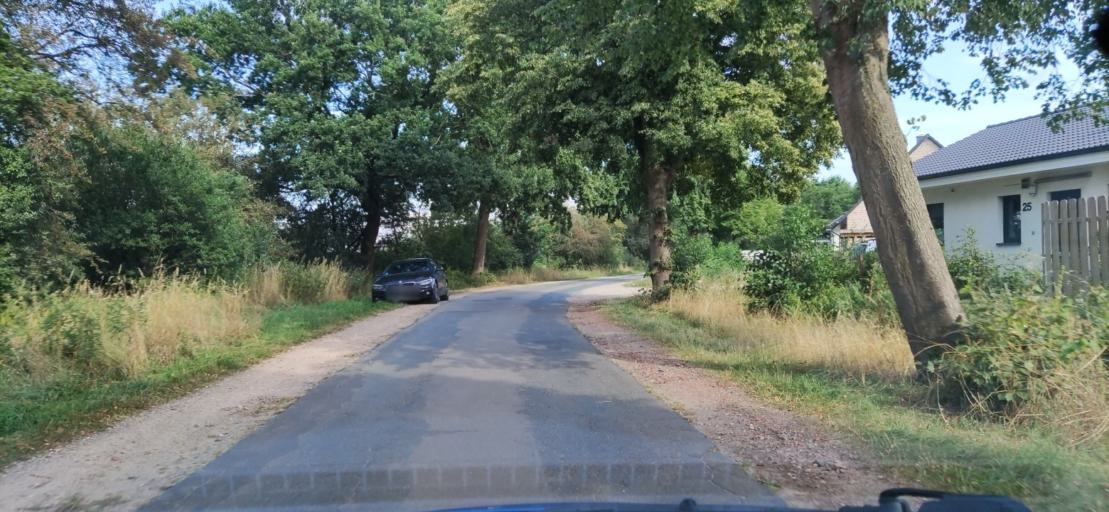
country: DE
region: Lower Saxony
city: Bleckede
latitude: 53.2888
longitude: 10.7210
